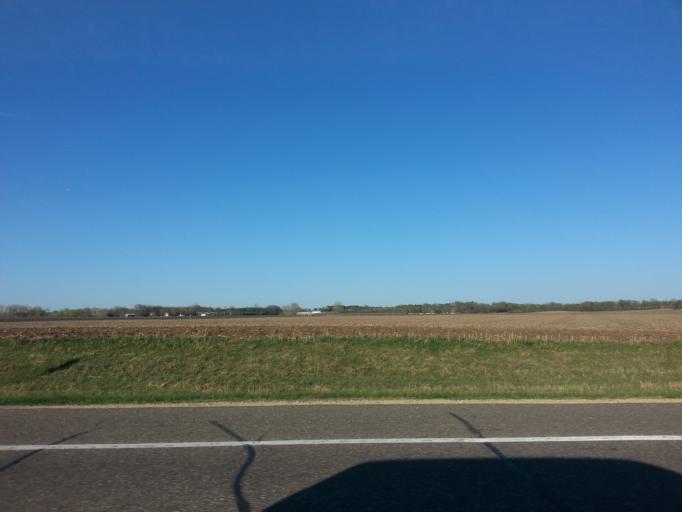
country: US
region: Minnesota
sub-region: Dakota County
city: Lakeville
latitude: 44.5855
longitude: -93.2165
